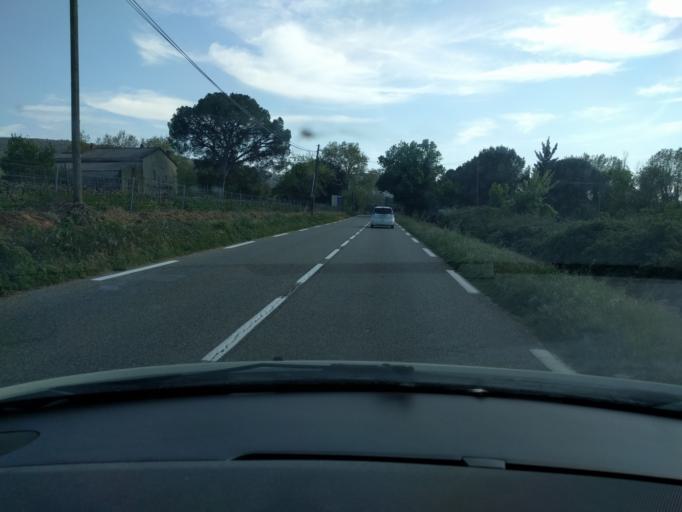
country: FR
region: Provence-Alpes-Cote d'Azur
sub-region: Departement du Var
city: Pierrefeu-du-Var
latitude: 43.2044
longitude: 6.1359
